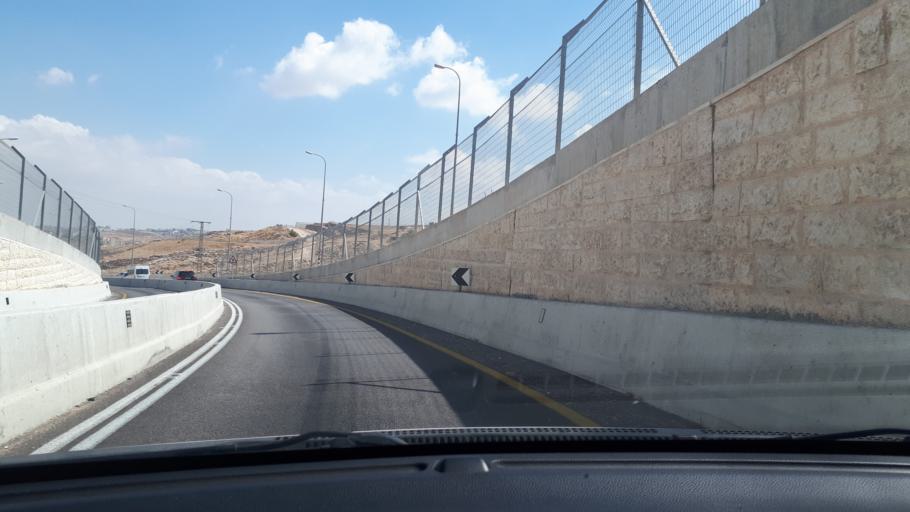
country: PS
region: West Bank
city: Jaba`
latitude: 31.8536
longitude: 35.2616
